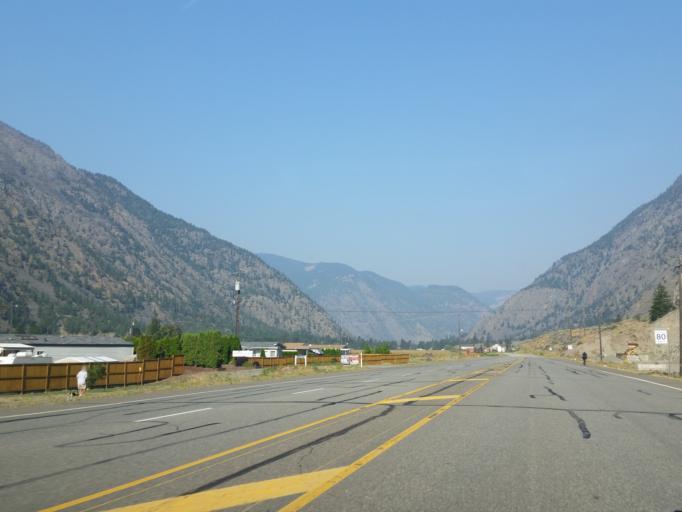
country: CA
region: British Columbia
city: Oliver
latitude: 49.2136
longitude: -119.9039
